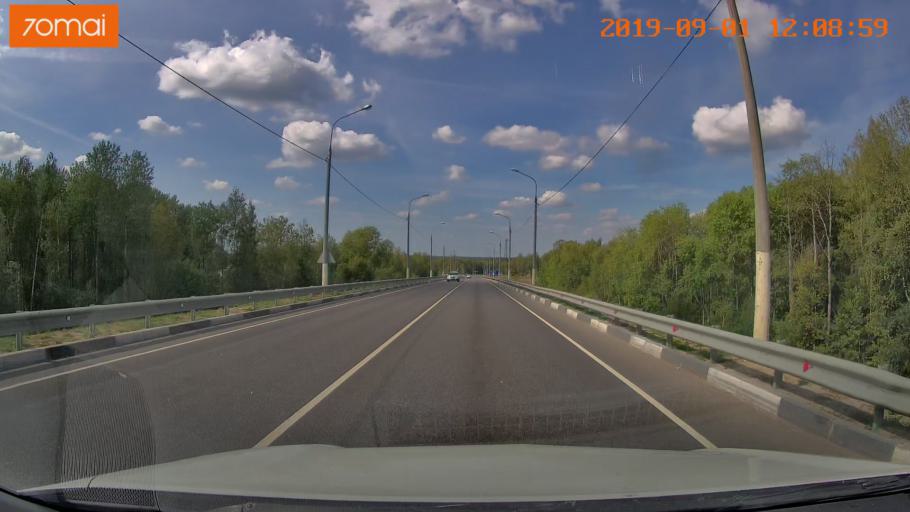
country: RU
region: Kaluga
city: Maloyaroslavets
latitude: 54.9792
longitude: 36.4320
